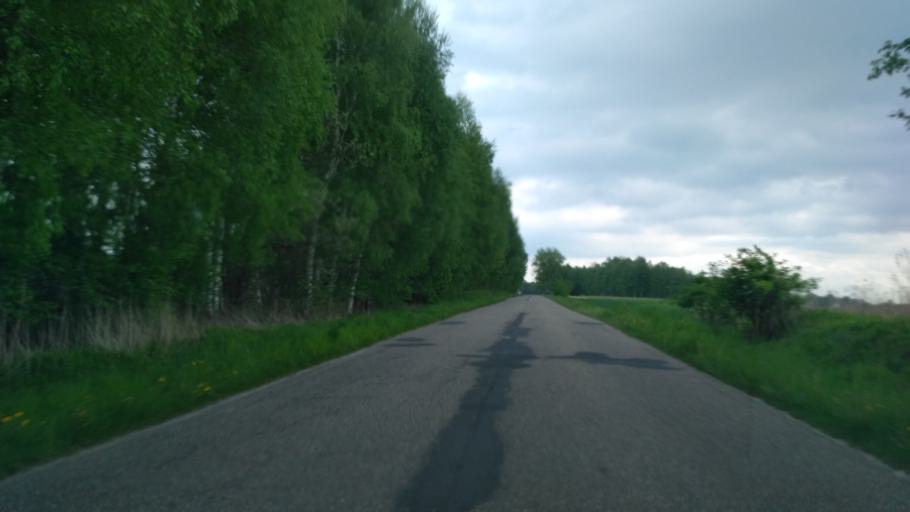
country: PL
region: Lesser Poland Voivodeship
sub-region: Powiat tarnowski
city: Szynwald
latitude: 49.9838
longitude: 21.1336
